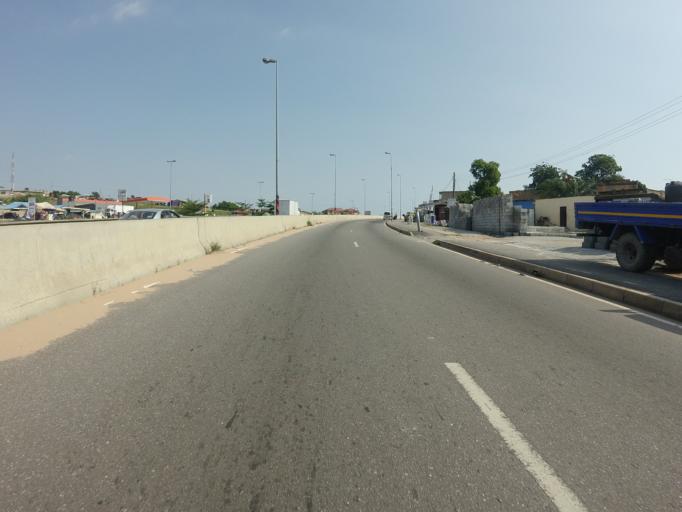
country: GH
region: Greater Accra
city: Gbawe
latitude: 5.6193
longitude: -0.2954
